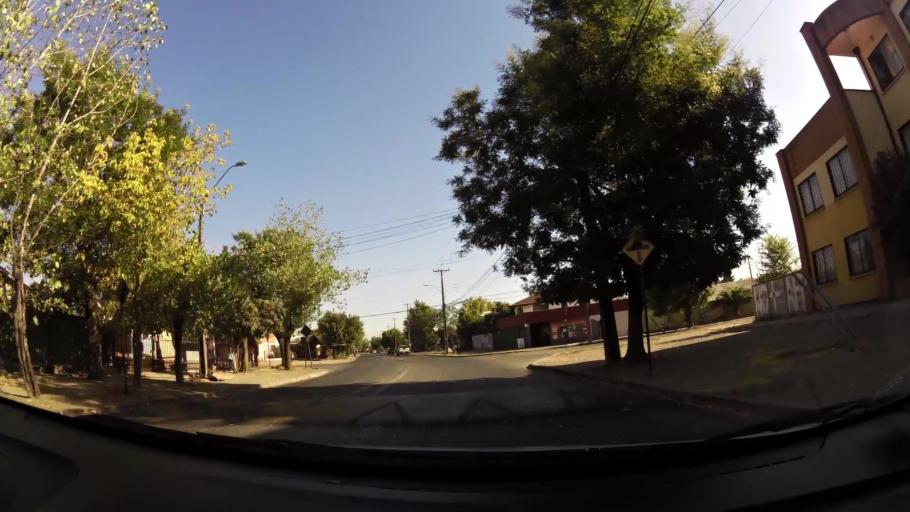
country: CL
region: Maule
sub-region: Provincia de Talca
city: Talca
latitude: -35.4378
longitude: -71.6705
